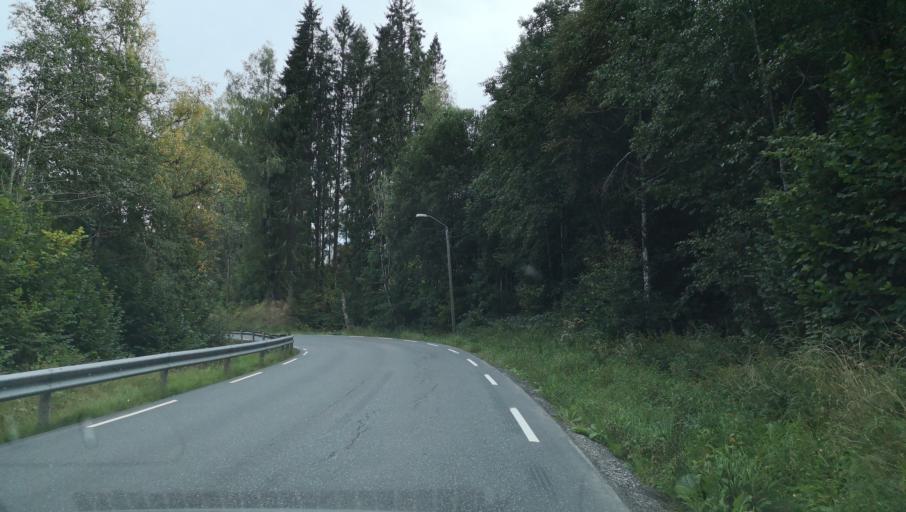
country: NO
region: Ostfold
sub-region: Hobol
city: Tomter
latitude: 59.6789
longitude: 11.0299
